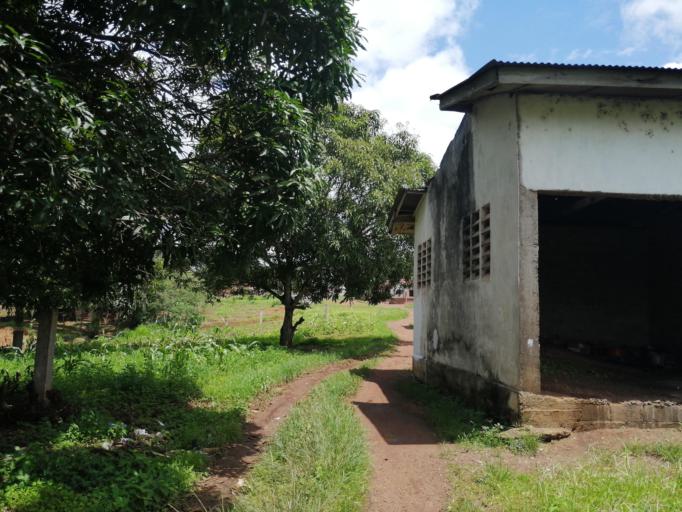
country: SL
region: Northern Province
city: Port Loko
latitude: 8.7699
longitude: -12.7839
